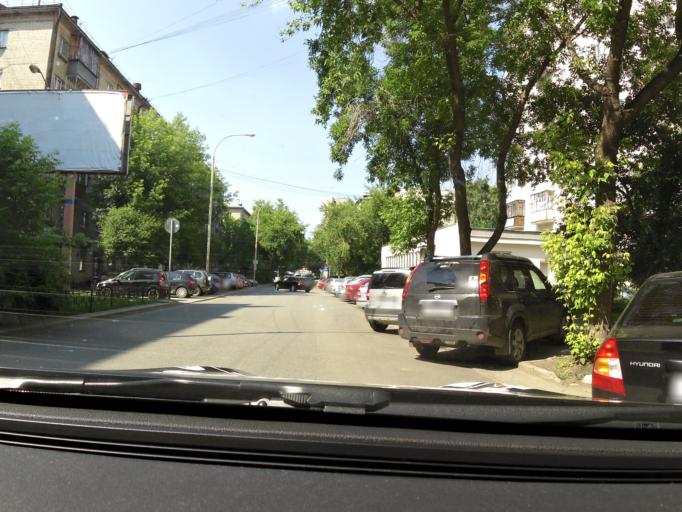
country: RU
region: Sverdlovsk
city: Yekaterinburg
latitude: 56.8334
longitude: 60.5864
